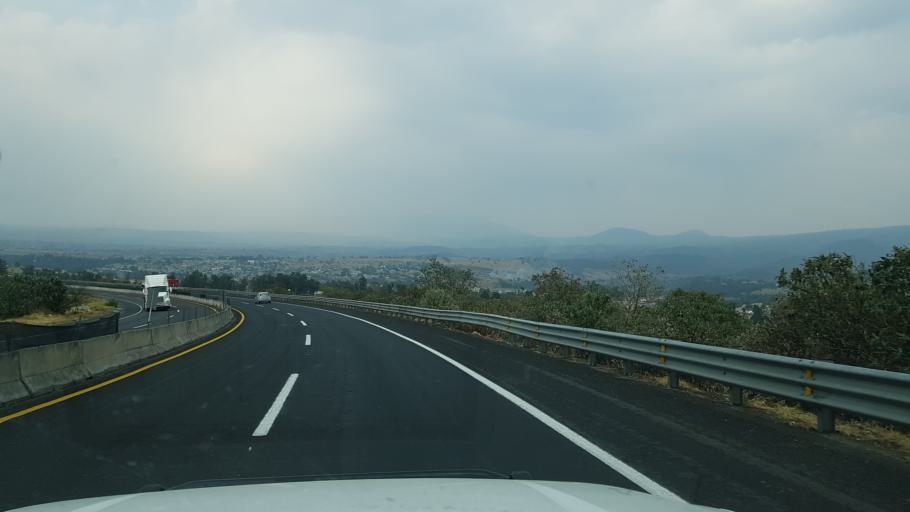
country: MX
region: Mexico
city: Tlalmanalco de Velazquez
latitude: 19.2002
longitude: -98.8129
